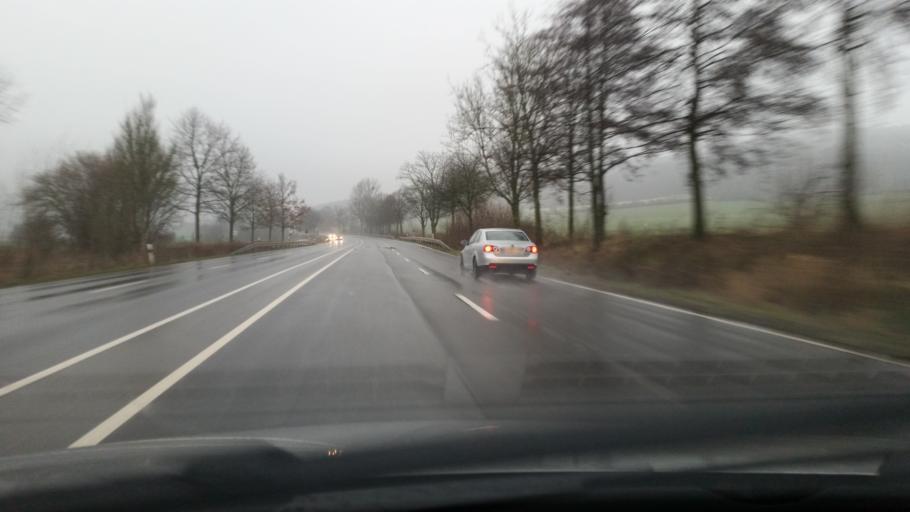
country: DE
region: Lower Saxony
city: Springe
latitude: 52.1872
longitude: 9.5284
